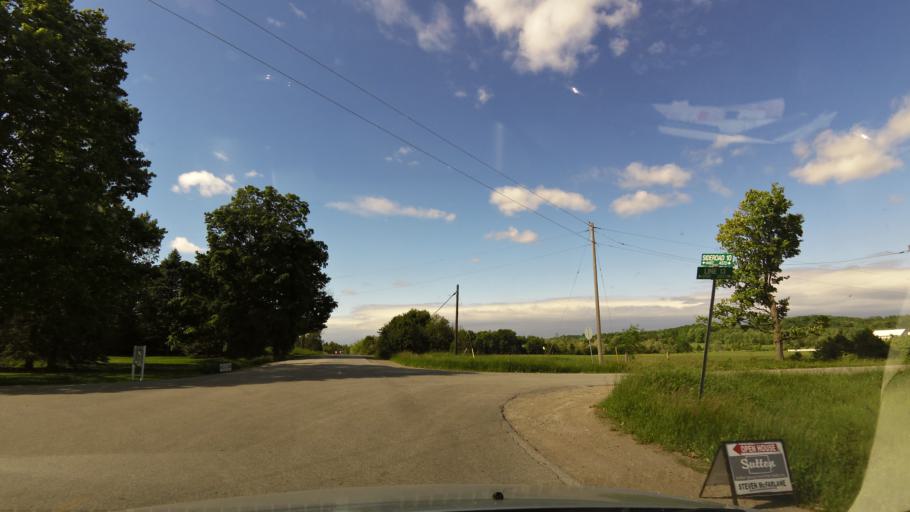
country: CA
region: Ontario
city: Bradford West Gwillimbury
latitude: 44.1792
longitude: -79.6199
